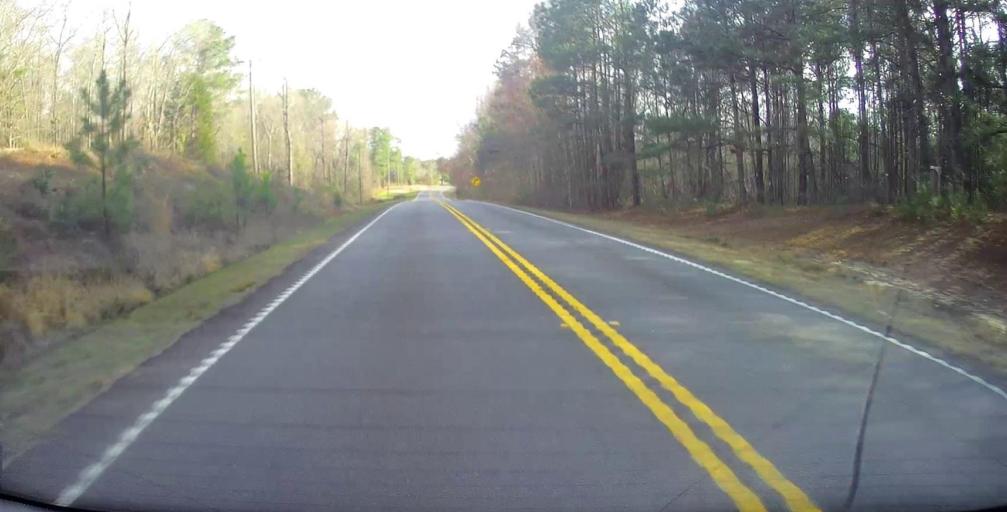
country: US
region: Georgia
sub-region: Talbot County
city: Talbotton
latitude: 32.5467
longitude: -84.6020
